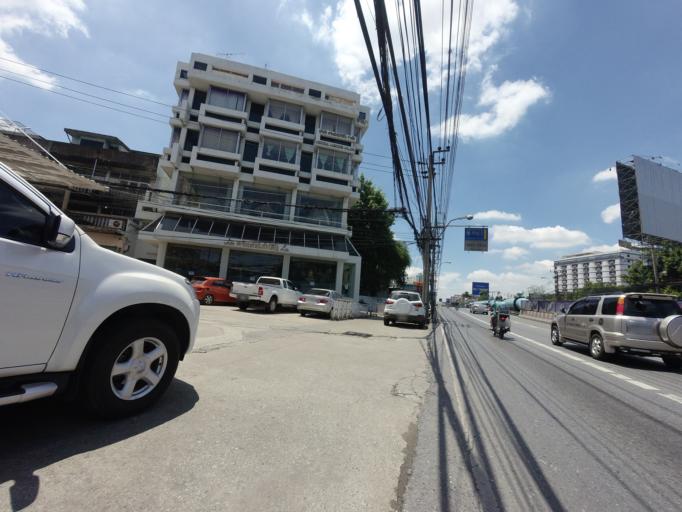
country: TH
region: Bangkok
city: Lat Phrao
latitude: 13.7979
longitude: 100.5885
